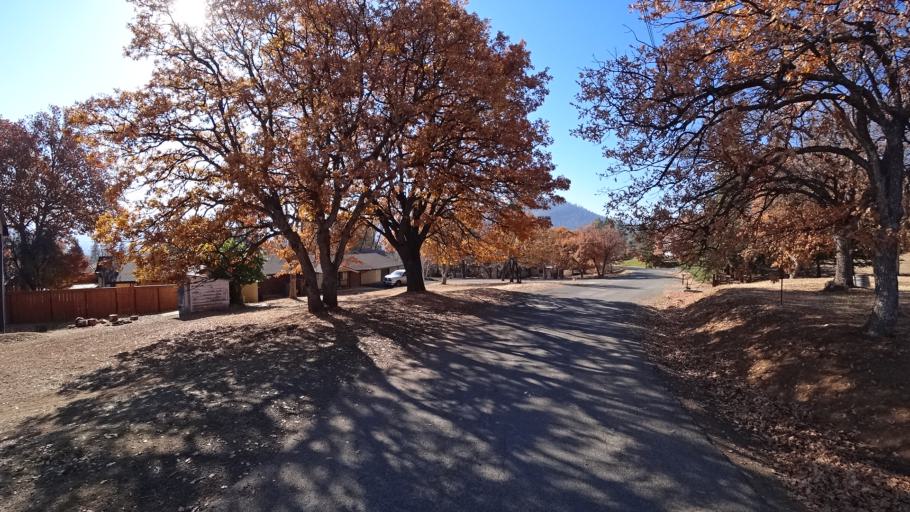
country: US
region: California
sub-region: Siskiyou County
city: Yreka
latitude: 41.7415
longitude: -122.6557
